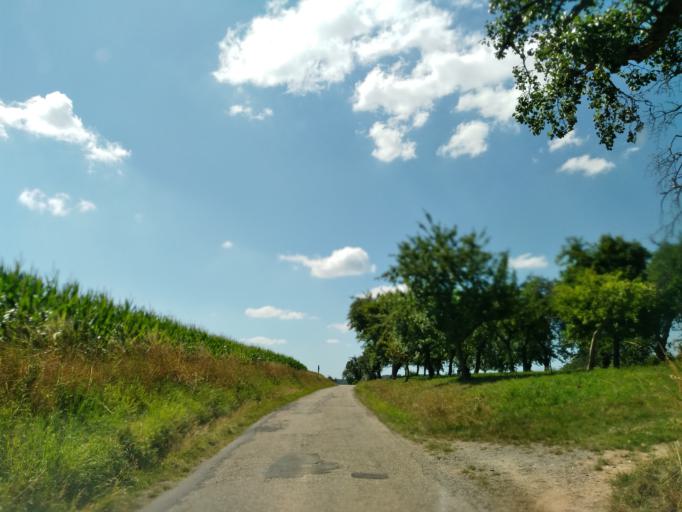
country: DE
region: Baden-Wuerttemberg
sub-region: Karlsruhe Region
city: Limbach
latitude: 49.4548
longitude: 9.2410
